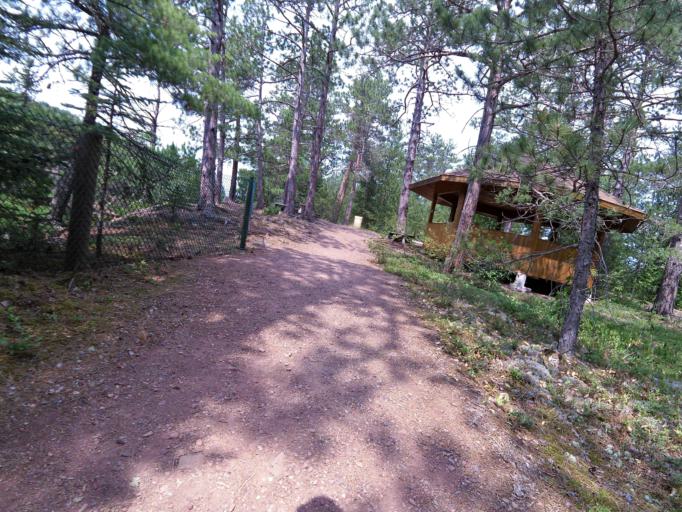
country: CA
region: Ontario
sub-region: Thunder Bay District
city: Thunder Bay
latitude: 48.7989
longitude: -88.6177
